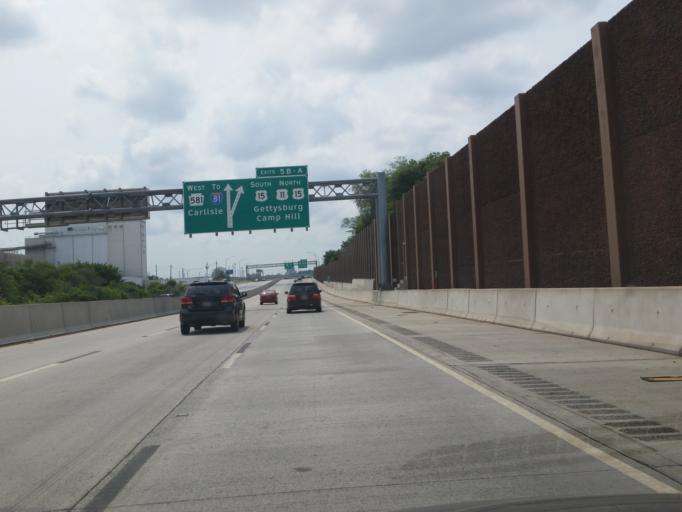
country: US
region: Pennsylvania
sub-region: Cumberland County
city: Camp Hill
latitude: 40.2336
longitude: -76.9220
